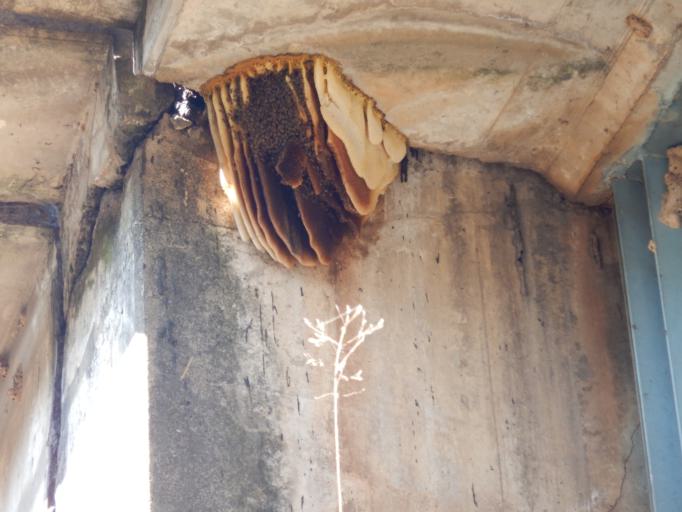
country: AR
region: Entre Rios
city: Parana
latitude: -31.6737
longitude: -60.5770
